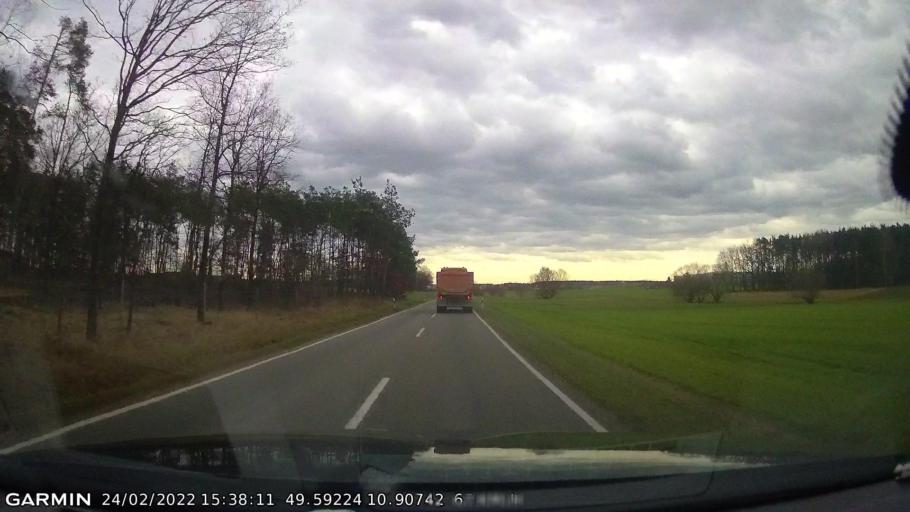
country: DE
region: Bavaria
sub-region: Regierungsbezirk Mittelfranken
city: Herzogenaurach
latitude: 49.5923
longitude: 10.9073
